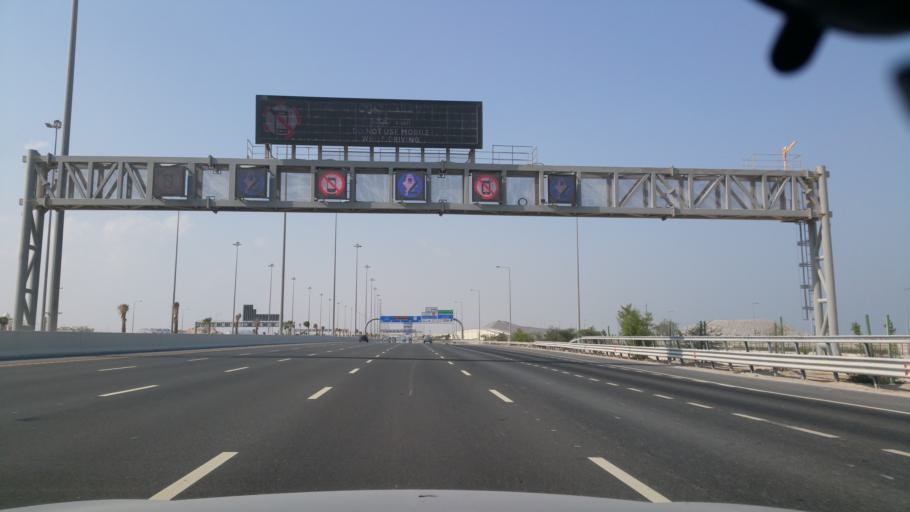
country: QA
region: Baladiyat Umm Salal
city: Umm Salal Muhammad
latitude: 25.4417
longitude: 51.4819
